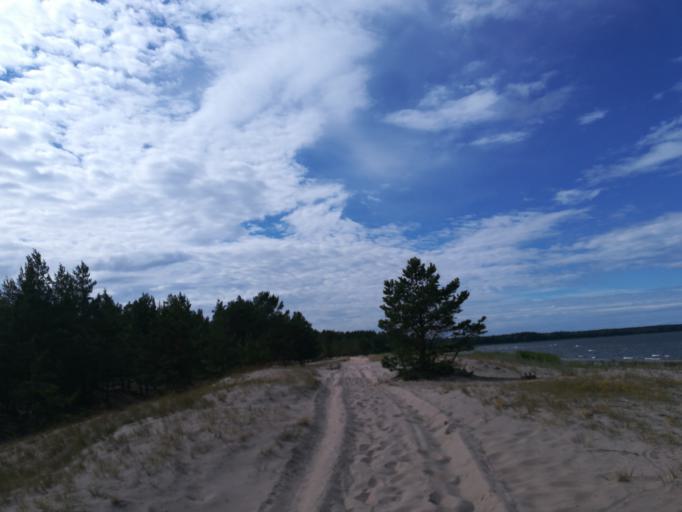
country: RU
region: Leningrad
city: Ust'-Luga
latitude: 59.6799
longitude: 28.2361
